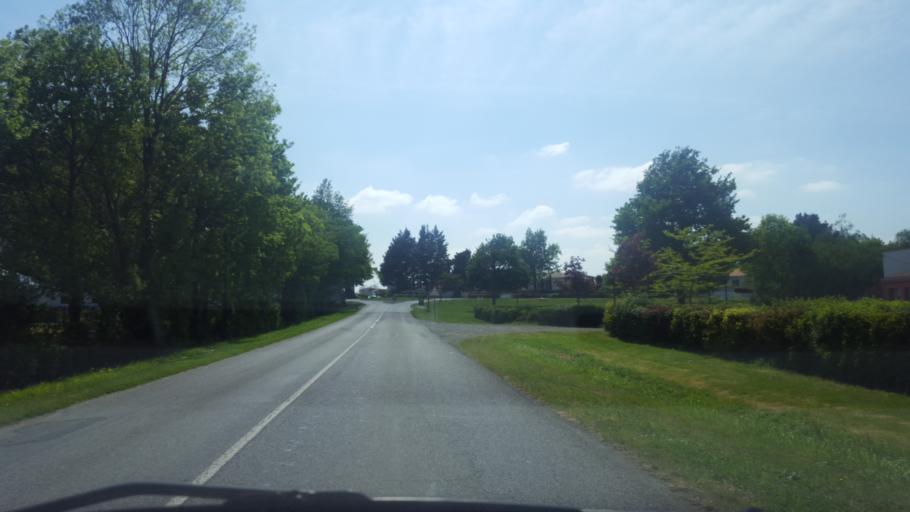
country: FR
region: Pays de la Loire
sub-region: Departement de la Loire-Atlantique
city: La Limouziniere
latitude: 46.9716
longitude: -1.5733
